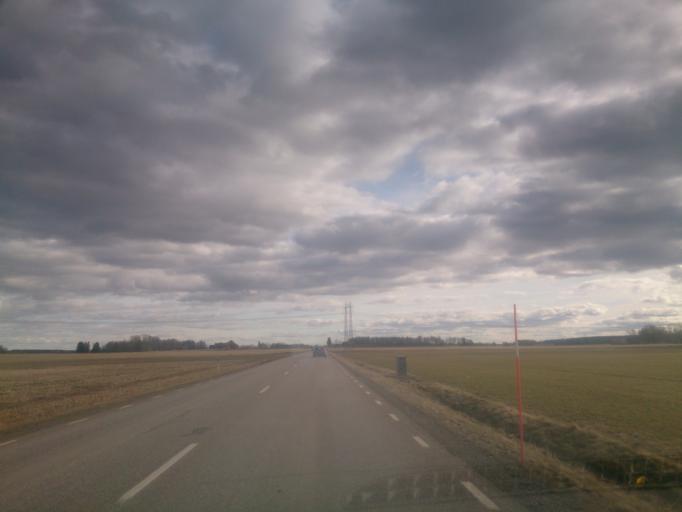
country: SE
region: OEstergoetland
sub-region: Motala Kommun
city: Borensberg
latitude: 58.5083
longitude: 15.1971
